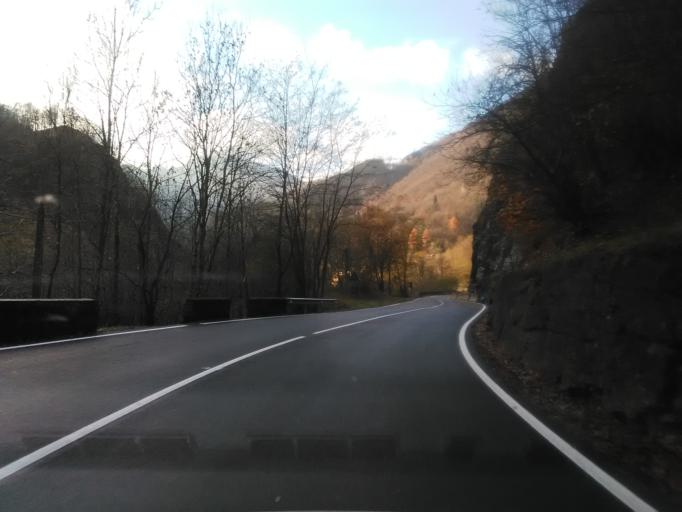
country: IT
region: Piedmont
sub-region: Provincia di Vercelli
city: Cravagliana
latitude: 45.8488
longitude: 8.2108
